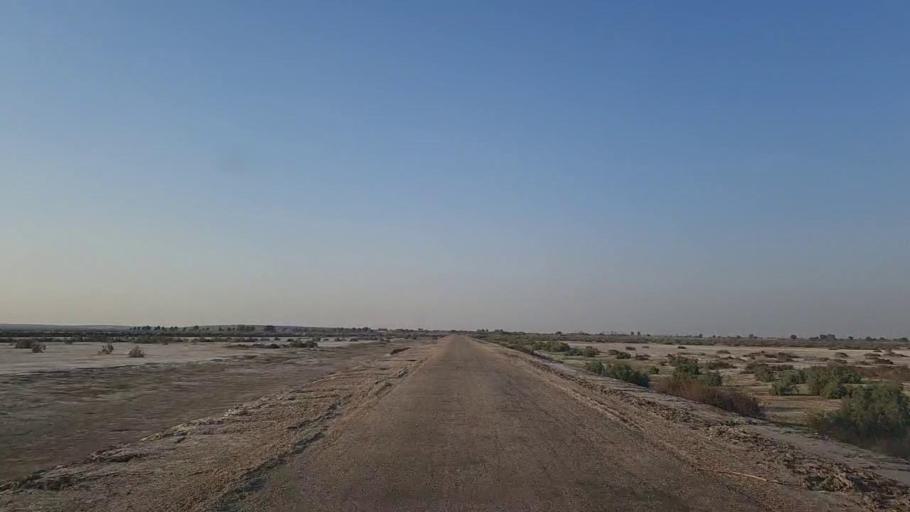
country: PK
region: Sindh
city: Jam Sahib
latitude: 26.3232
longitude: 68.6681
